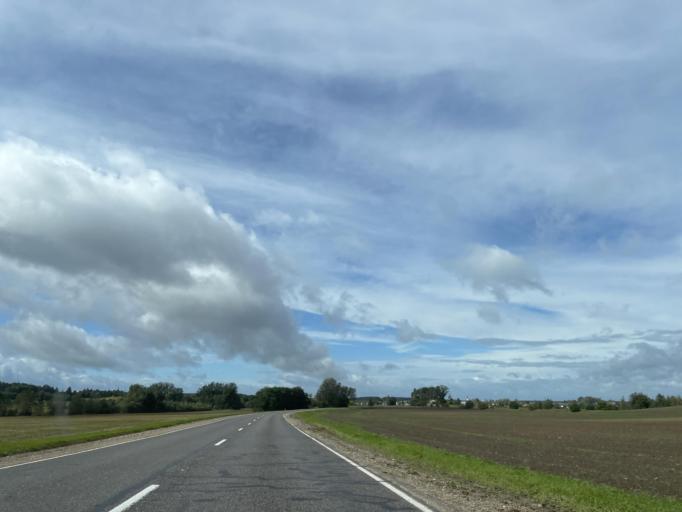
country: BY
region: Brest
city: Kosava
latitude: 52.7444
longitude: 25.1832
